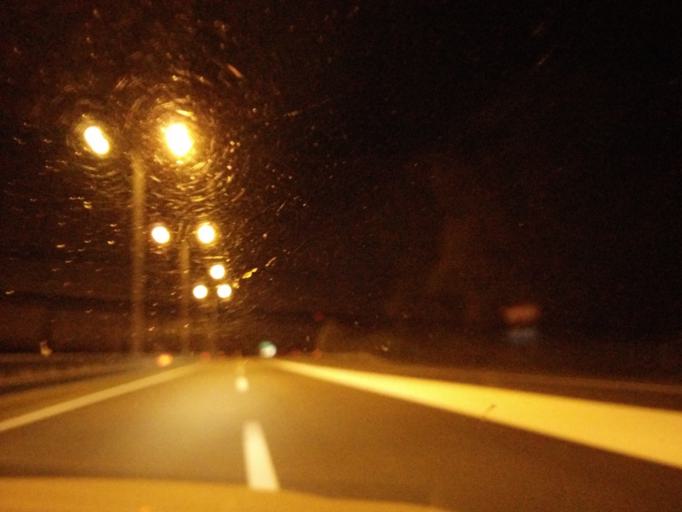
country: HR
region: Brodsko-Posavska
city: Vrpolje
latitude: 45.1450
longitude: 18.3012
